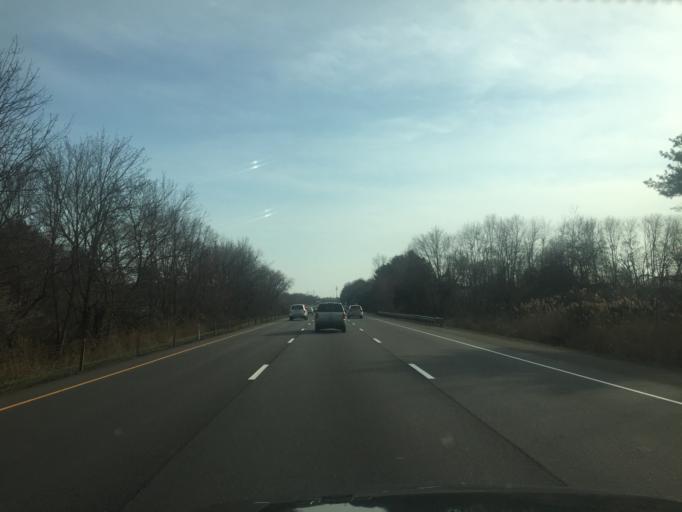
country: US
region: Connecticut
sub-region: New Haven County
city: Wallingford Center
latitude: 41.4440
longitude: -72.7916
